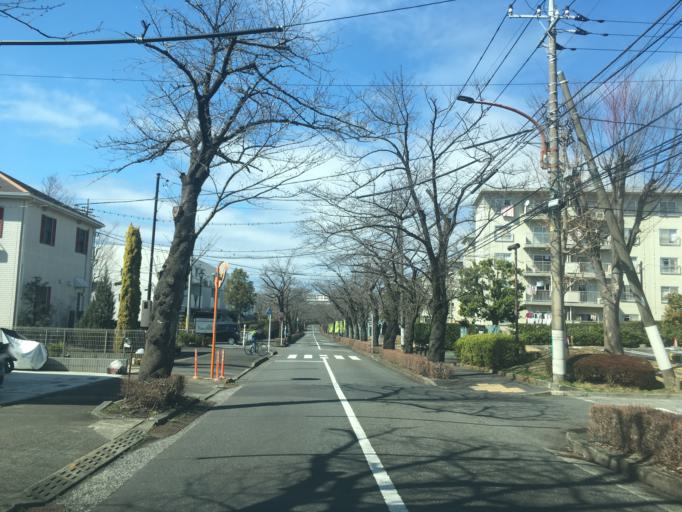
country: JP
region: Tokyo
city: Hino
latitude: 35.6183
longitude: 139.4488
